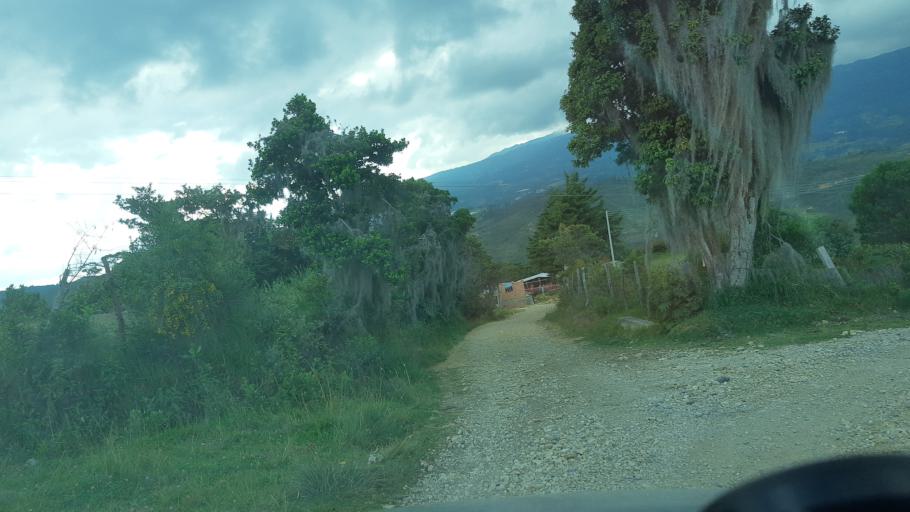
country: CO
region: Boyaca
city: Santa Sofia
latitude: 5.7439
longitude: -73.5688
